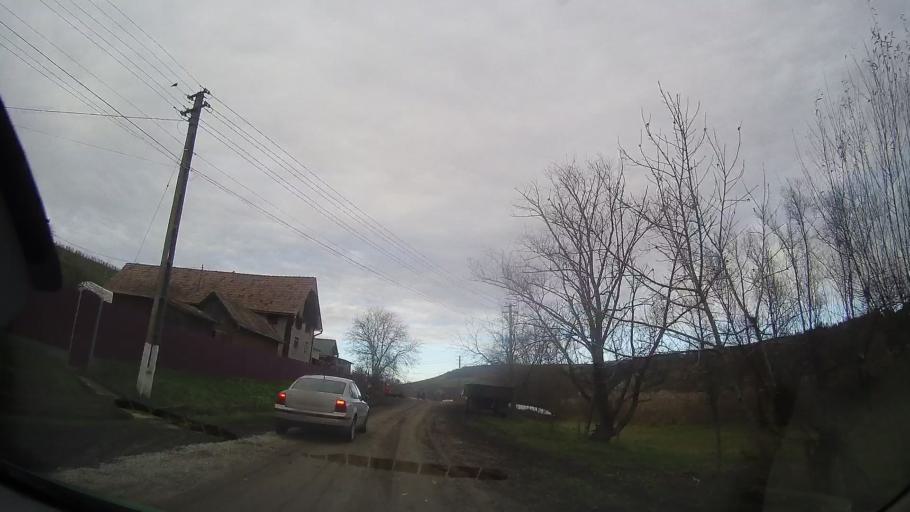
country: RO
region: Cluj
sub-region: Comuna Geaca
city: Geaca
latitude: 46.8570
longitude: 24.0864
